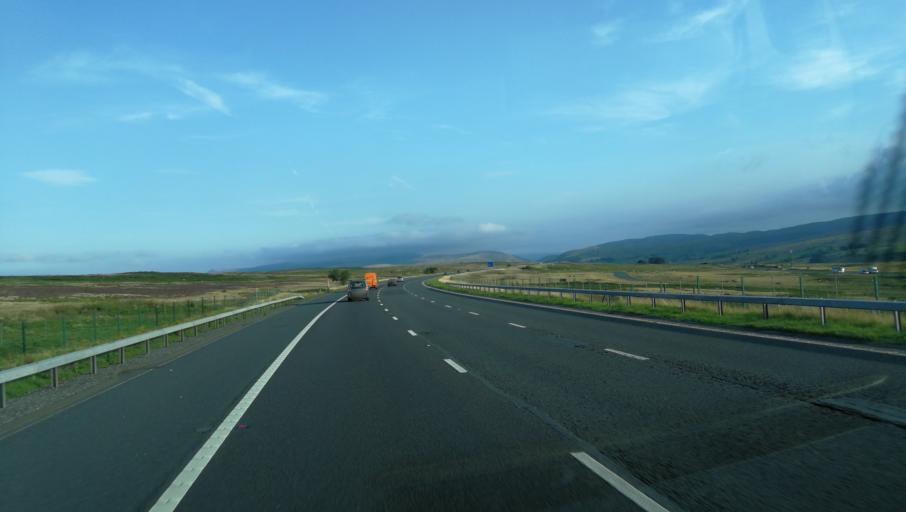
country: GB
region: England
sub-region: Cumbria
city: Appleby-in-Westmorland
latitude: 54.4861
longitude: -2.6355
